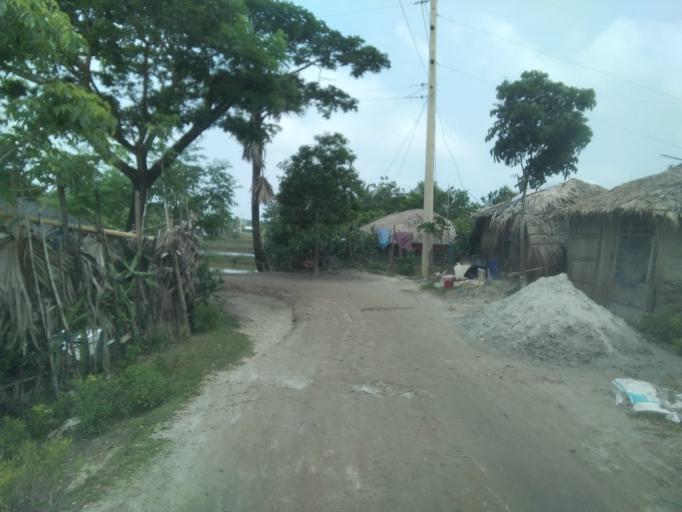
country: BD
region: Khulna
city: Phultala
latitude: 22.6425
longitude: 89.4294
